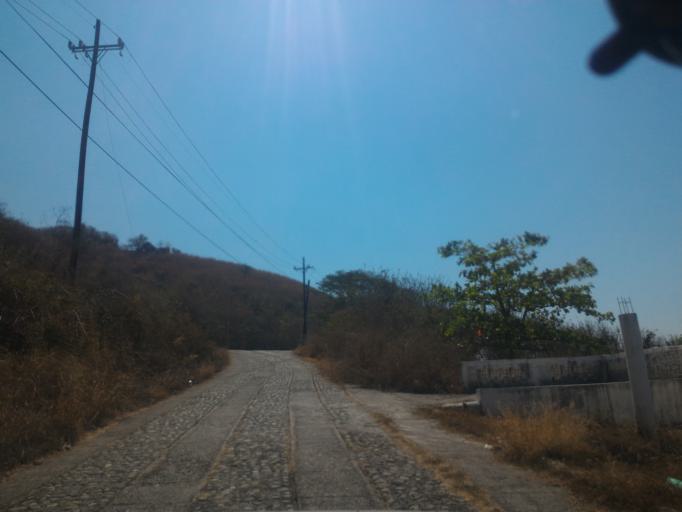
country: MX
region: Michoacan
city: Coahuayana Viejo
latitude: 18.5749
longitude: -103.6627
